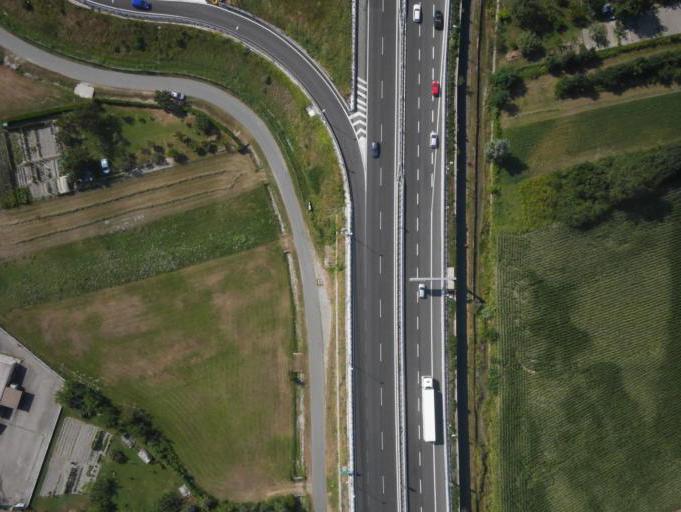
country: IT
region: Piedmont
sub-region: Provincia di Torino
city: Avigliana
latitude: 45.0931
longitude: 7.4018
